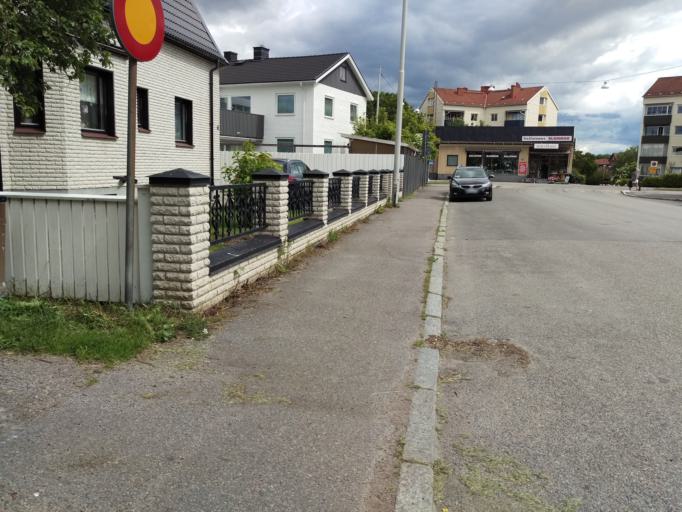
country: SE
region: OEstergoetland
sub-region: Norrkopings Kommun
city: Norrkoping
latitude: 58.5790
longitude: 16.1942
